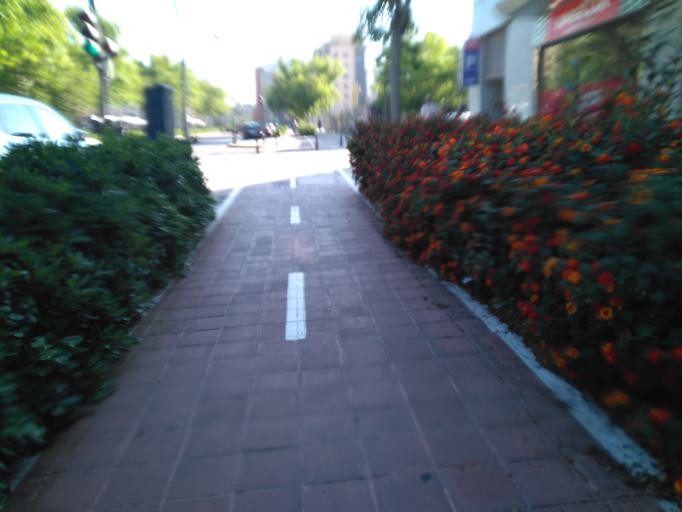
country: ES
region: Valencia
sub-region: Provincia de Valencia
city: Tavernes Blanques
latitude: 39.4898
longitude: -0.3659
